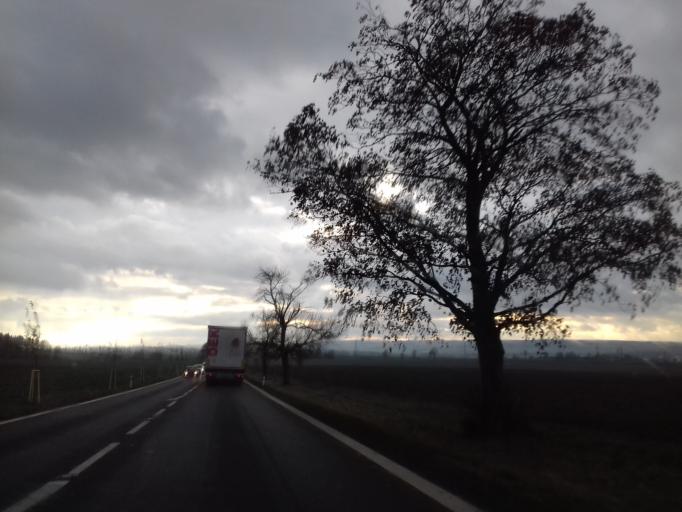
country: CZ
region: Pardubicky
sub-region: Okres Svitavy
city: Svitavy
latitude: 49.7667
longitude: 16.5153
